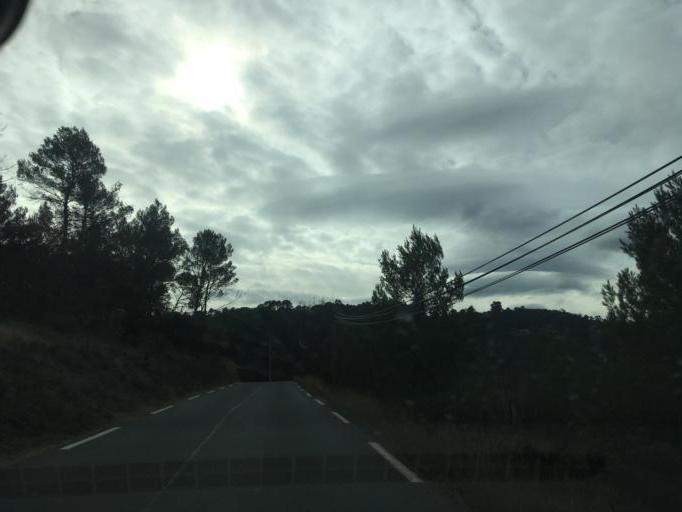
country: FR
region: Provence-Alpes-Cote d'Azur
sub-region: Departement du Var
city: Bras
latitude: 43.4641
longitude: 5.9639
